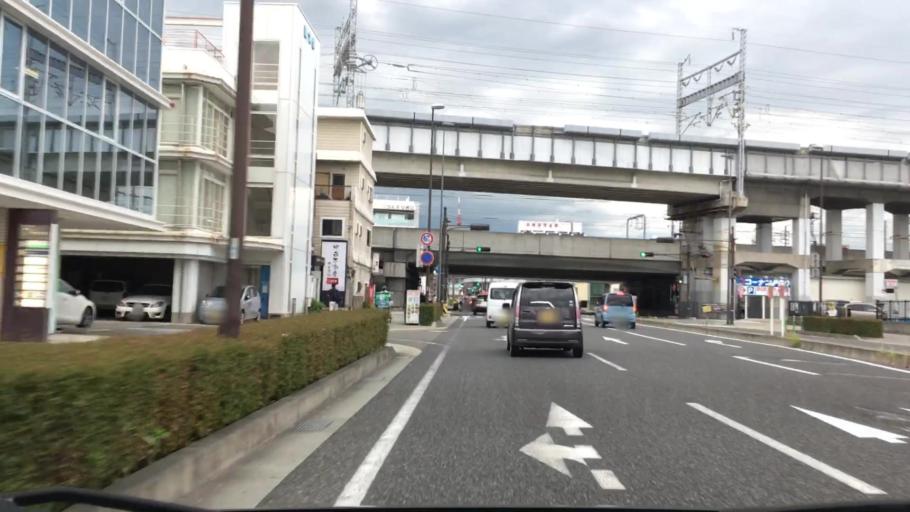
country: JP
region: Hyogo
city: Himeji
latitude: 34.8253
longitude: 134.6949
